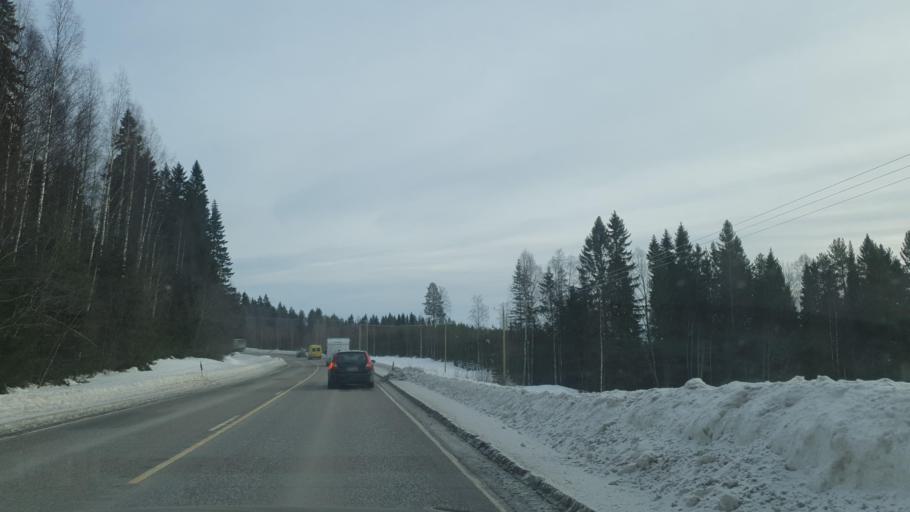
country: FI
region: Kainuu
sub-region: Kajaani
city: Kajaani
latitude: 64.4283
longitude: 27.5818
